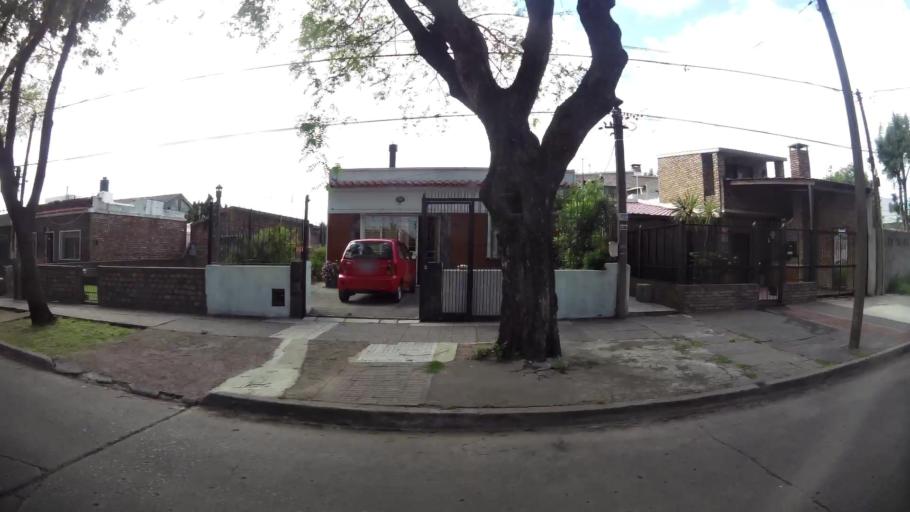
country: UY
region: Montevideo
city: Montevideo
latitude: -34.8687
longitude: -56.1576
